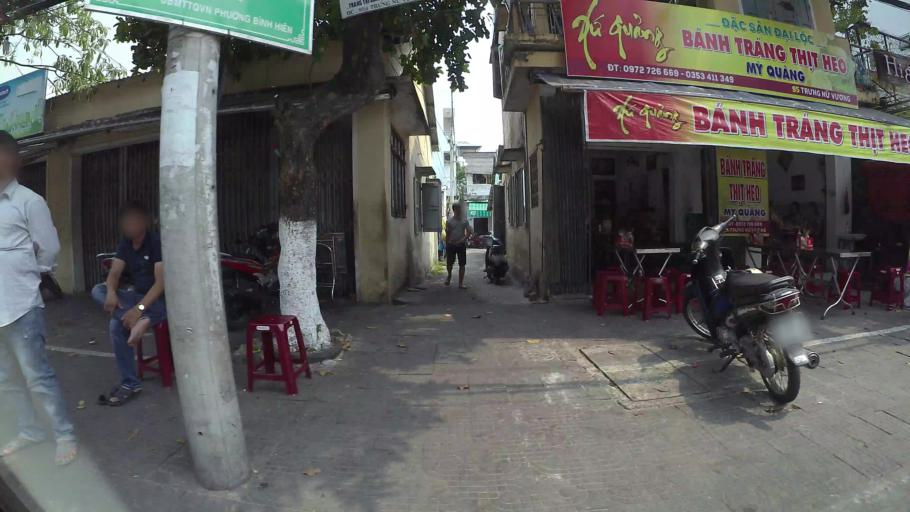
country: VN
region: Da Nang
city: Da Nang
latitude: 16.0580
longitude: 108.2208
